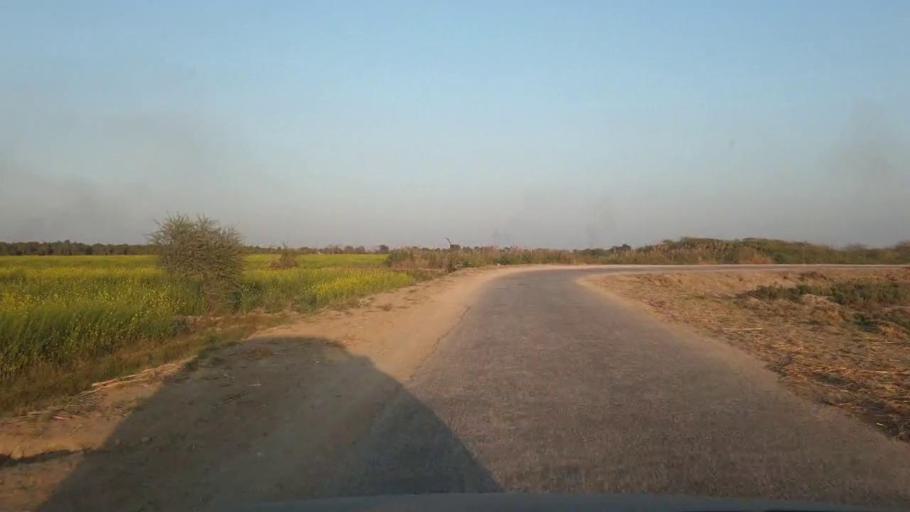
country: PK
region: Sindh
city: Mirwah Gorchani
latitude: 25.2792
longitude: 68.9387
